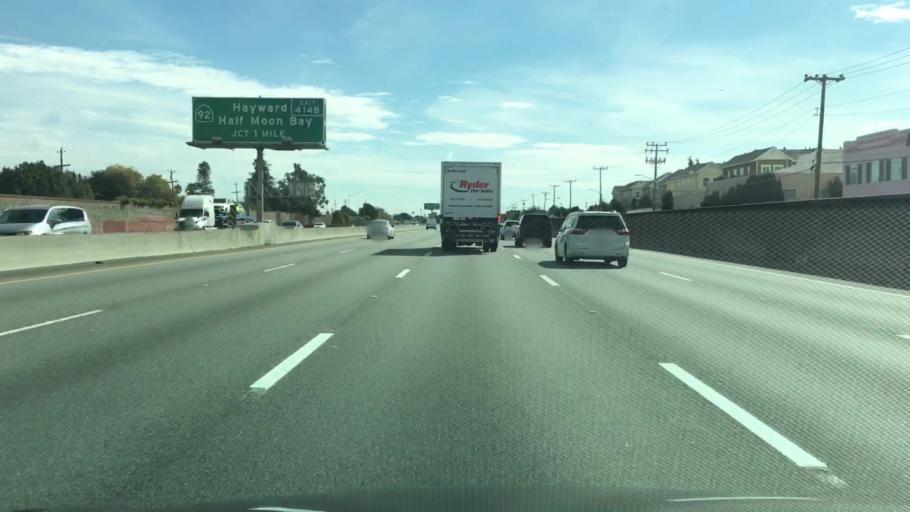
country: US
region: California
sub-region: San Mateo County
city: San Mateo
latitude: 37.5658
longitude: -122.3102
